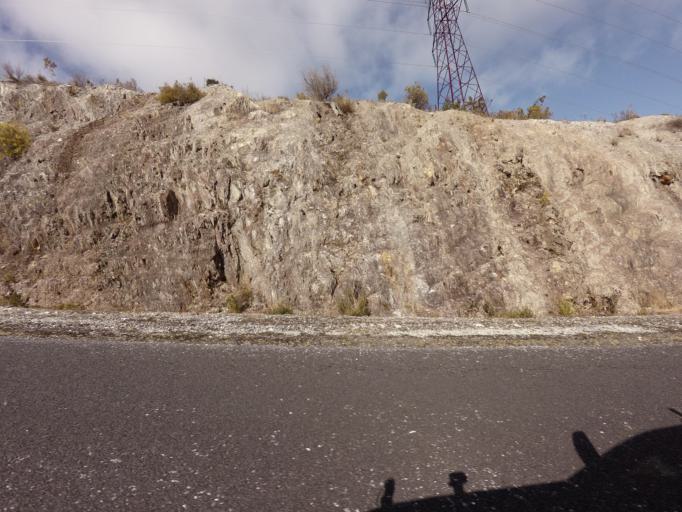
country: AU
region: Tasmania
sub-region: Huon Valley
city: Geeveston
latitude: -42.8128
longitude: 146.0982
